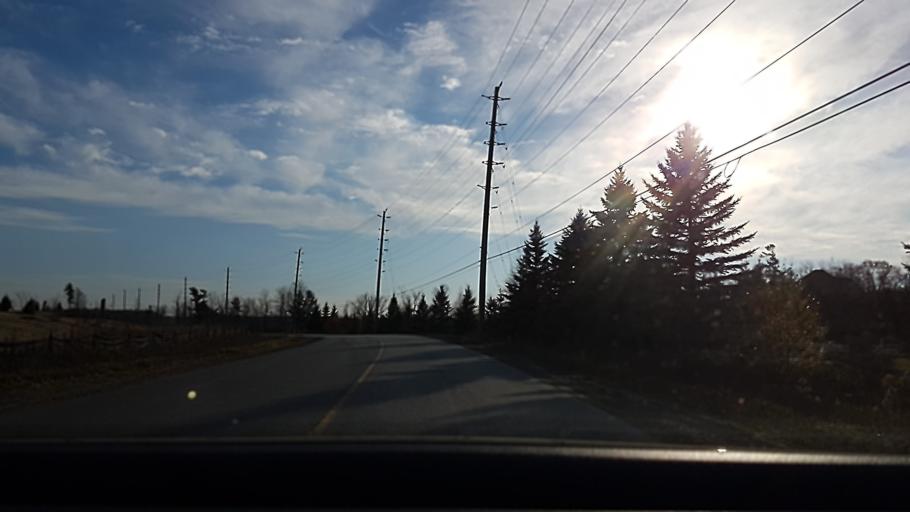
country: CA
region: Ontario
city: Barrie
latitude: 44.3857
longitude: -79.5550
